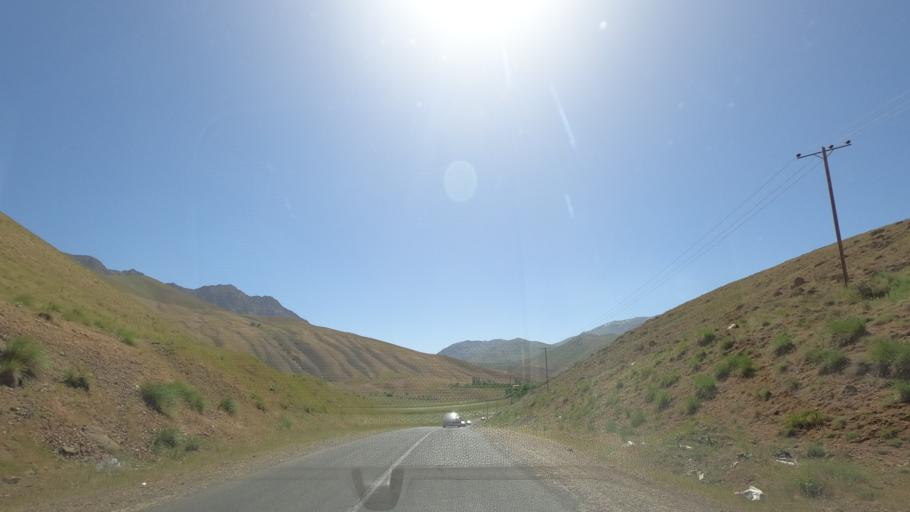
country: IR
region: Alborz
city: Karaj
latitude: 35.9258
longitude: 51.1019
